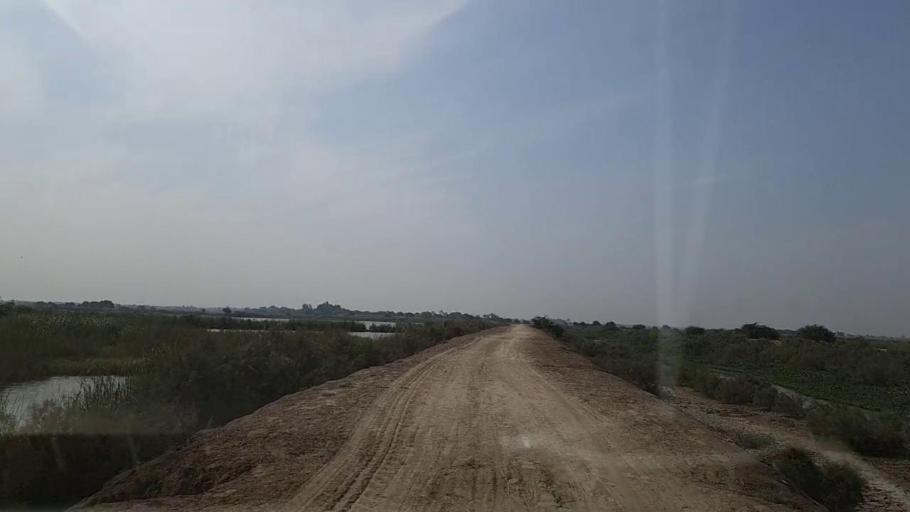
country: PK
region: Sindh
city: Mirpur Batoro
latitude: 24.6582
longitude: 68.2479
